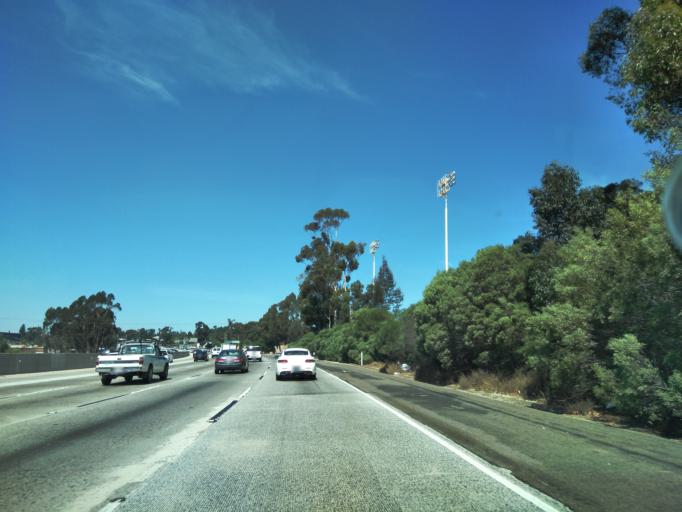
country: US
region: California
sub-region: Orange County
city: Mission Viejo
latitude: 33.5936
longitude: -117.6721
